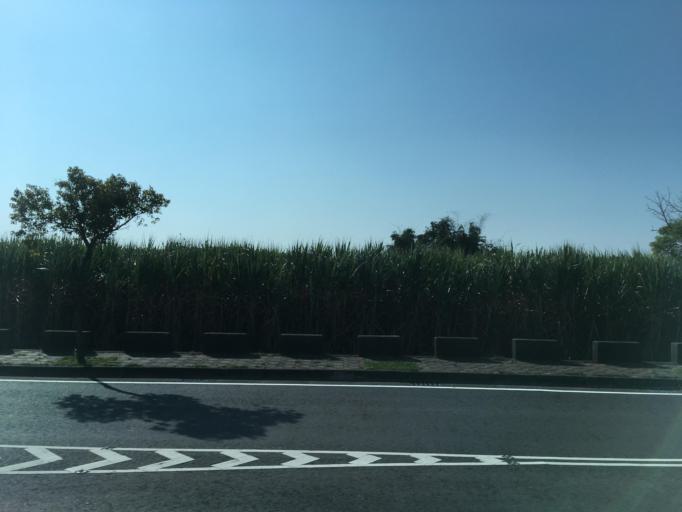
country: TW
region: Taiwan
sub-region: Chiayi
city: Taibao
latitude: 23.4828
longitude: 120.3586
